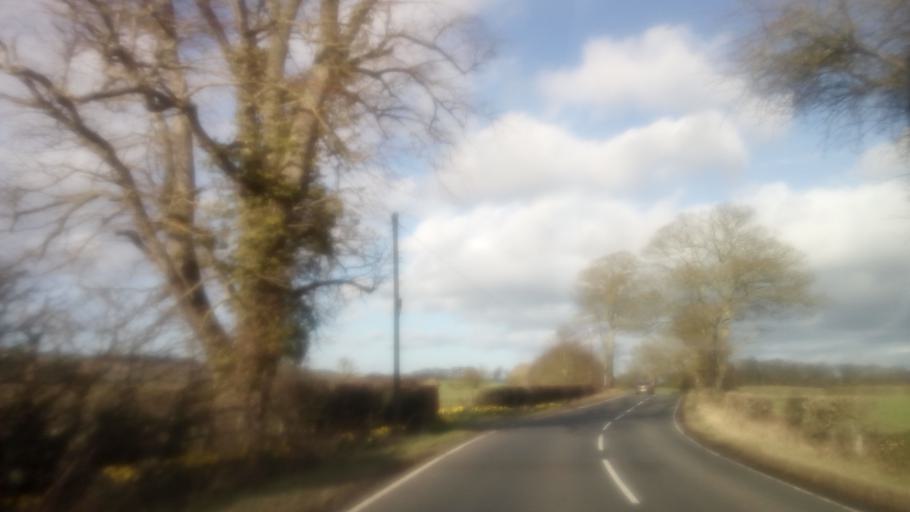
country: GB
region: Scotland
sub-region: The Scottish Borders
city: Jedburgh
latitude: 55.4751
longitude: -2.6436
